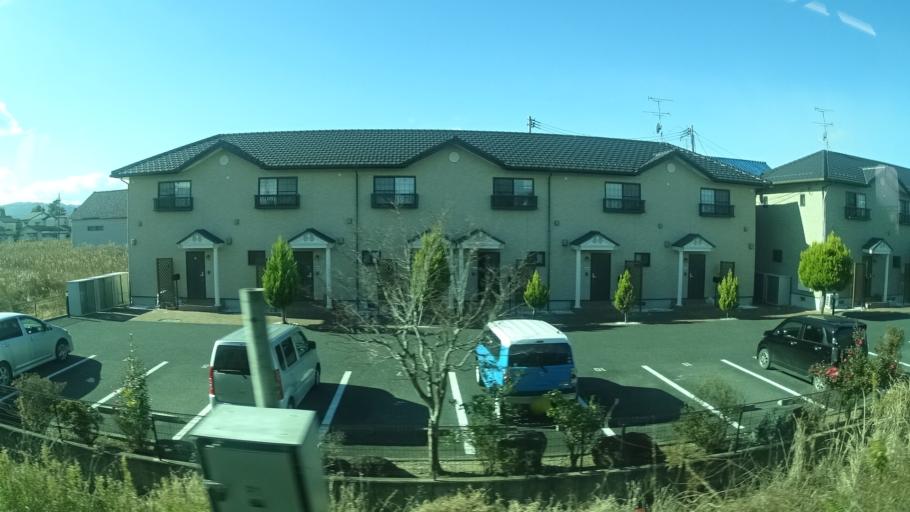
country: JP
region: Miyagi
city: Marumori
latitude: 37.7989
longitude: 140.9268
